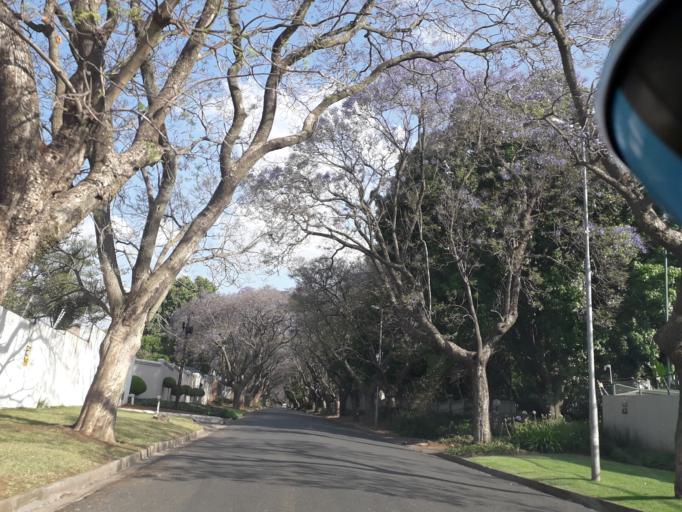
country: ZA
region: Gauteng
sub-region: City of Johannesburg Metropolitan Municipality
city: Johannesburg
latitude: -26.1334
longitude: 28.0736
